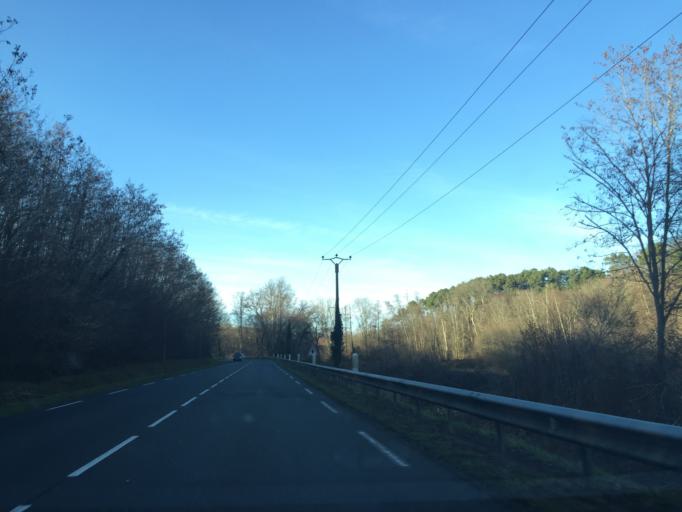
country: FR
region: Aquitaine
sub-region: Departement de la Dordogne
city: Riberac
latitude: 45.1735
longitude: 0.3906
